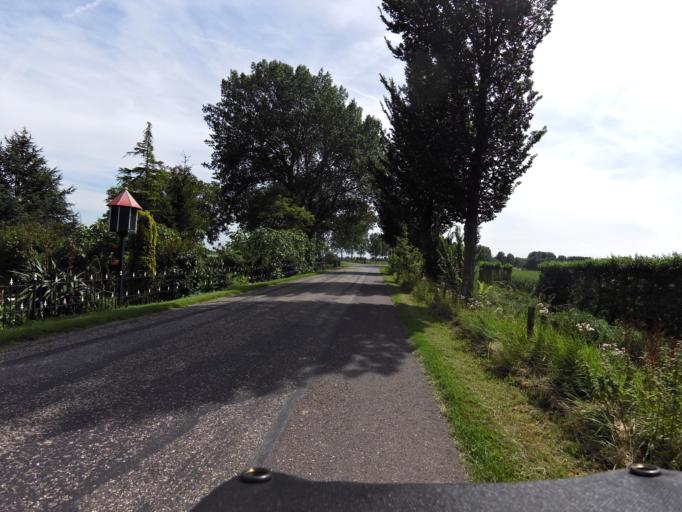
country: NL
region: South Holland
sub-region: Gemeente Goeree-Overflakkee
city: Dirksland
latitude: 51.7629
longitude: 4.1053
